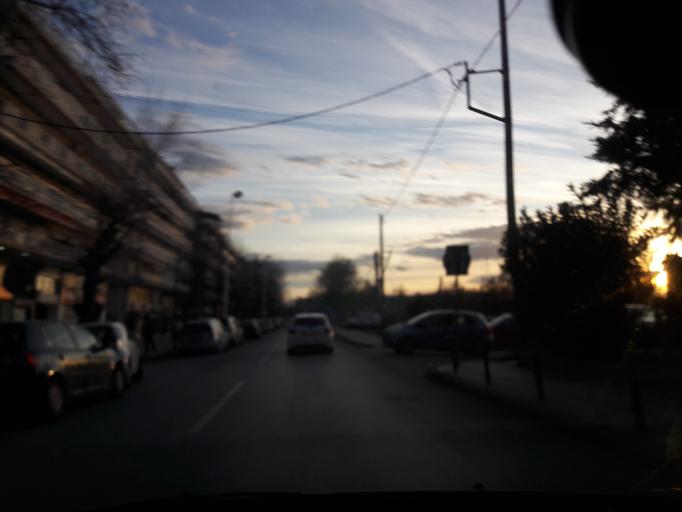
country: GR
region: Central Macedonia
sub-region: Nomos Thessalonikis
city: Kalamaria
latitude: 40.5887
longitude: 22.9444
